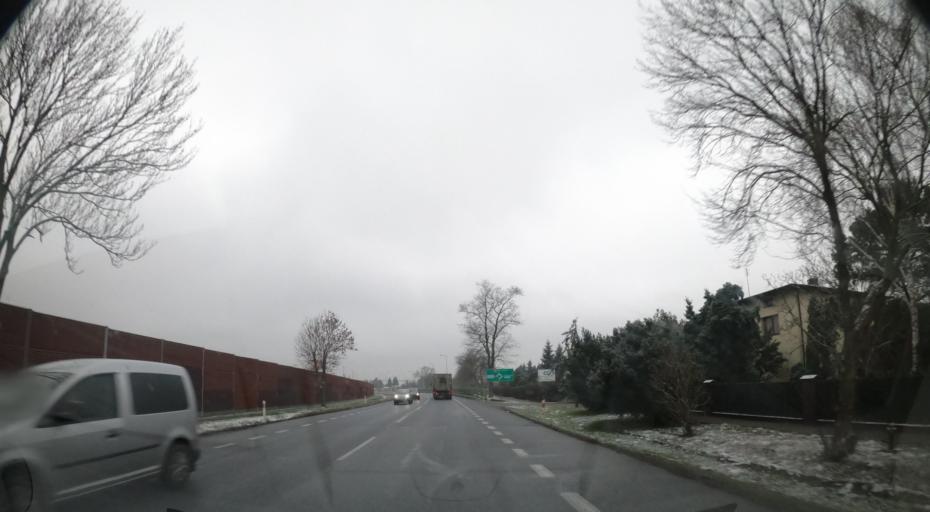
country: PL
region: Masovian Voivodeship
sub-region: Powiat sochaczewski
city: Sochaczew
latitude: 52.2264
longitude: 20.2715
